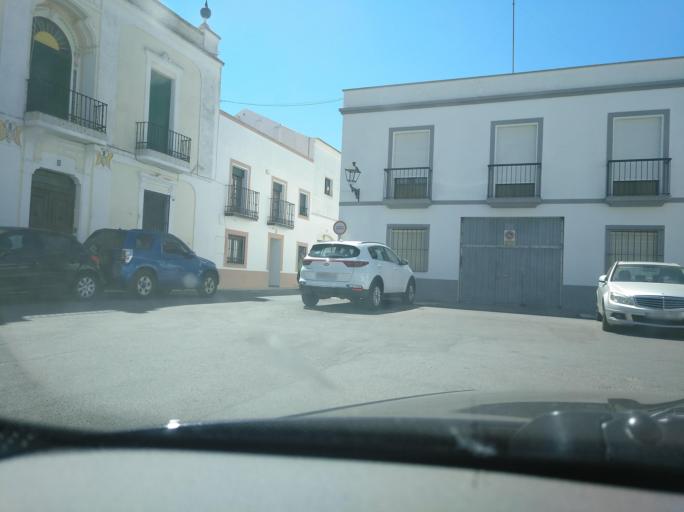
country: ES
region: Extremadura
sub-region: Provincia de Badajoz
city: Olivenza
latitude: 38.6861
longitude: -7.1022
